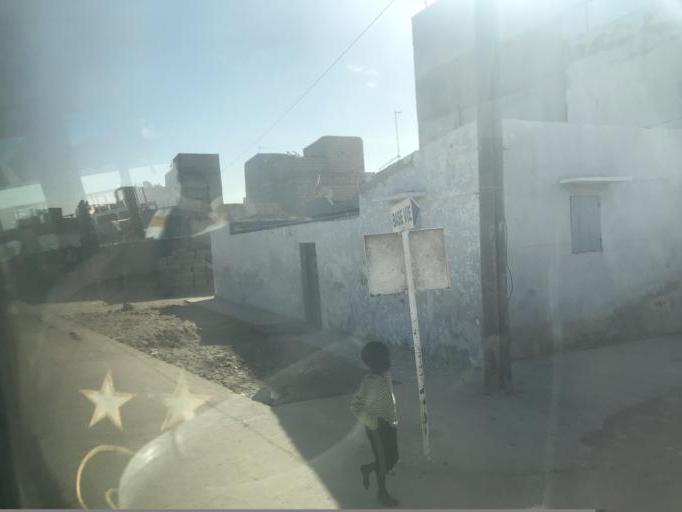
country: SN
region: Saint-Louis
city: Saint-Louis
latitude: 16.0468
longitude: -16.5058
